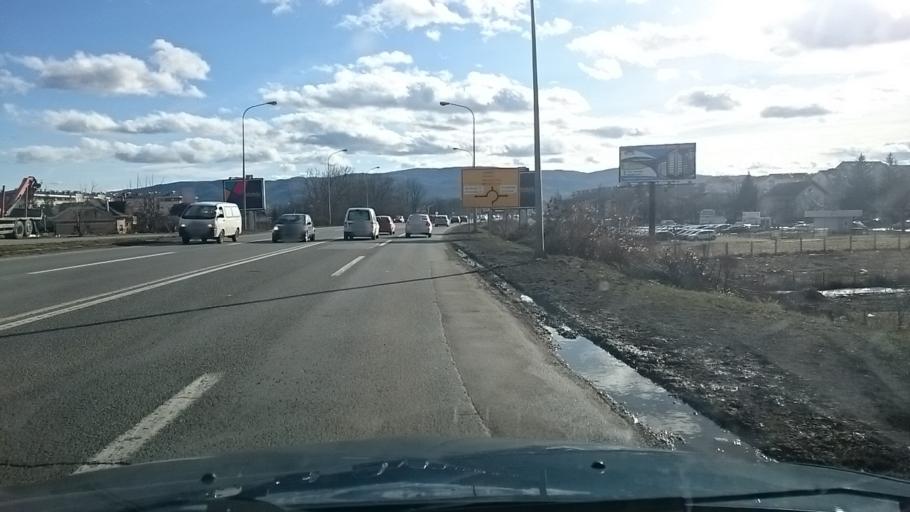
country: BA
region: Republika Srpska
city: Banja Luka
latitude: 44.7942
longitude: 17.1995
